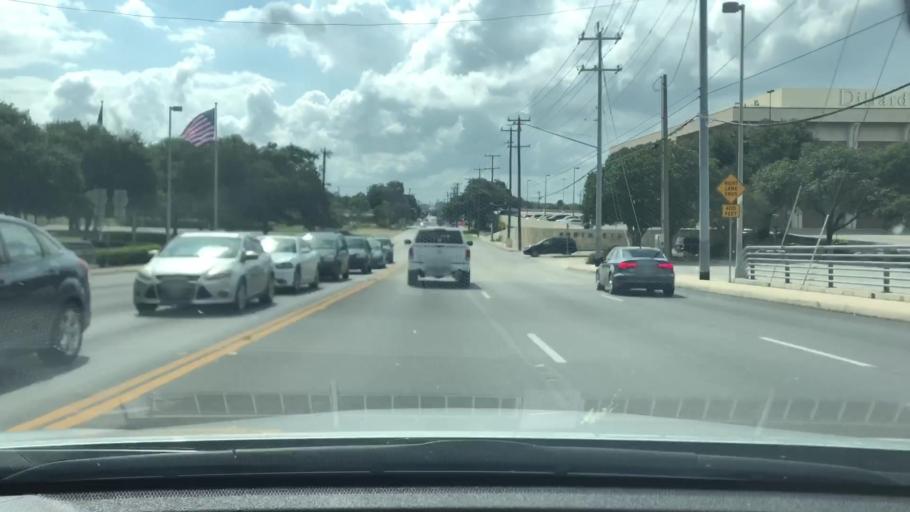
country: US
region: Texas
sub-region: Bexar County
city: Castle Hills
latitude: 29.5199
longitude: -98.4918
